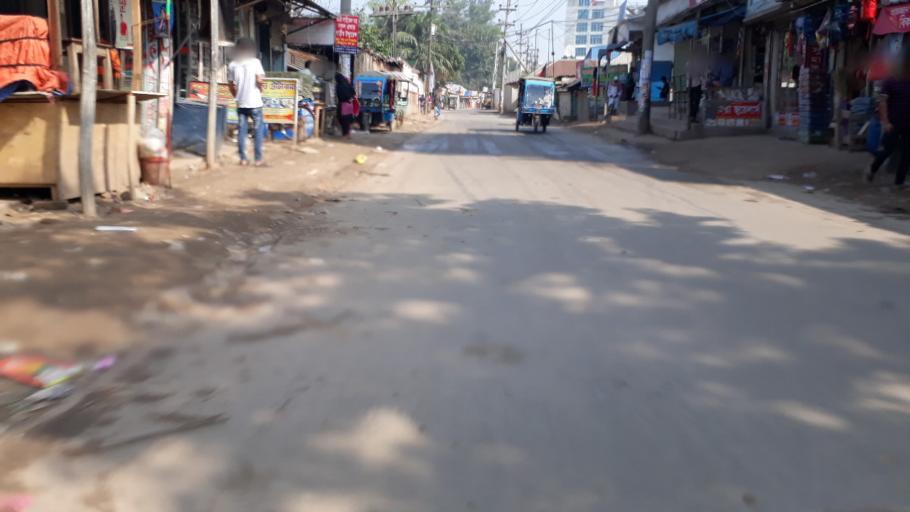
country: BD
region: Dhaka
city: Tungi
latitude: 23.8899
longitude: 90.3220
